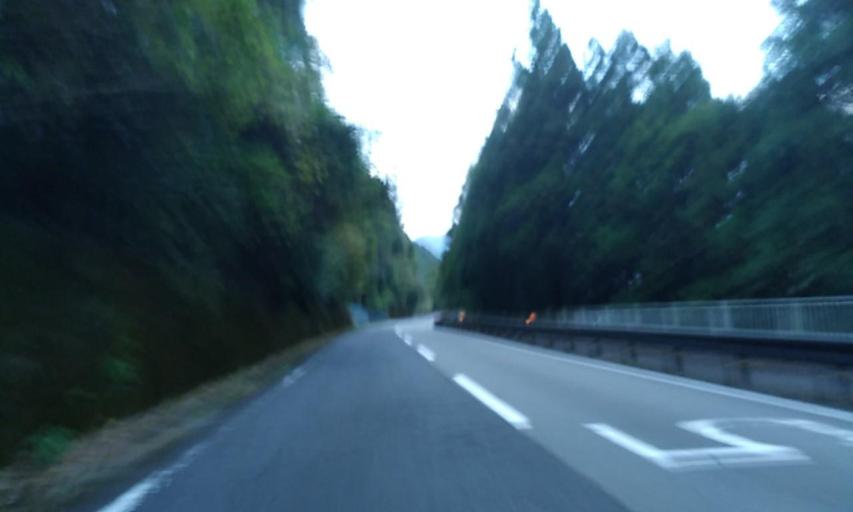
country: JP
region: Wakayama
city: Shingu
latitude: 33.7364
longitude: 135.9399
